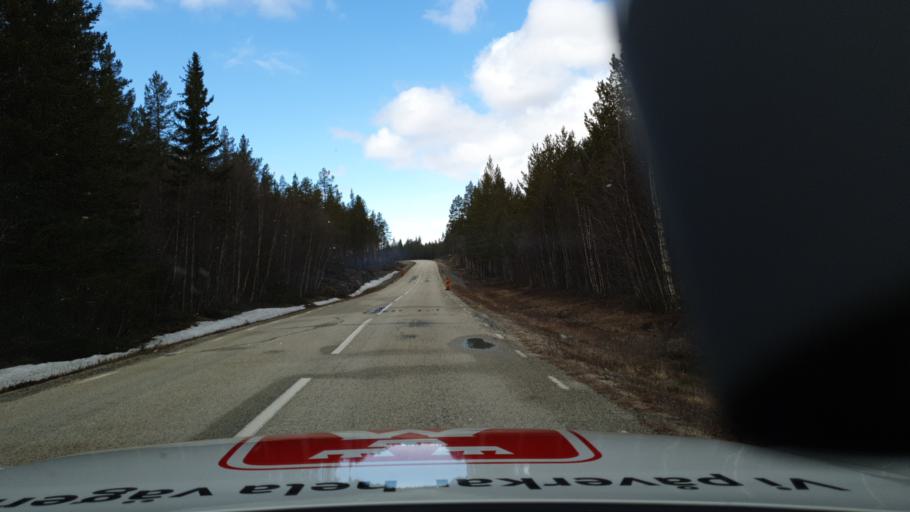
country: SE
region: Jaemtland
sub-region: Are Kommun
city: Jarpen
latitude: 62.8294
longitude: 13.4546
